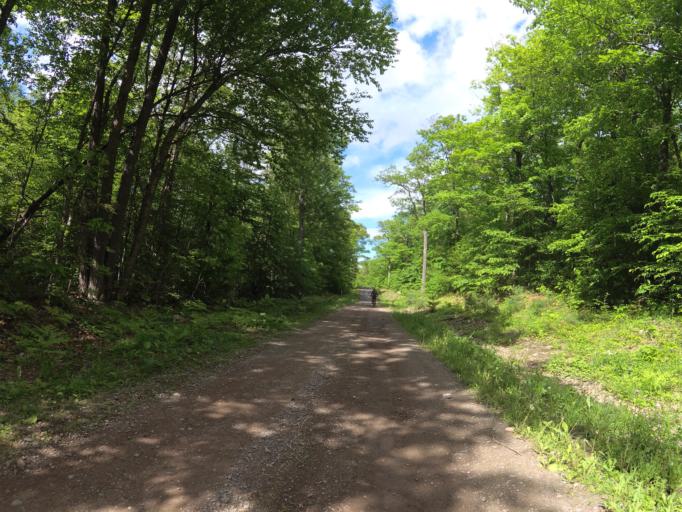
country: CA
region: Ontario
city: Renfrew
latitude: 45.1208
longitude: -76.8840
